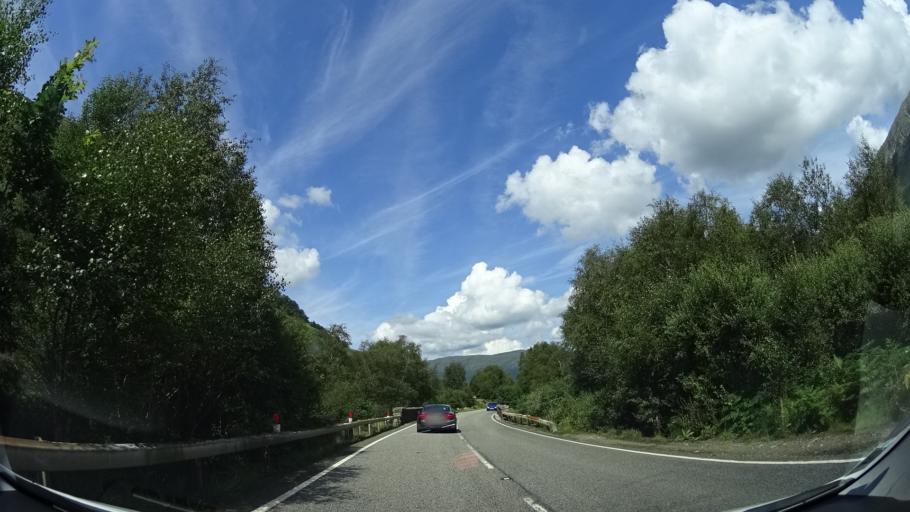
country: GB
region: Scotland
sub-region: Highland
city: Fort William
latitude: 56.6614
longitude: -5.0701
